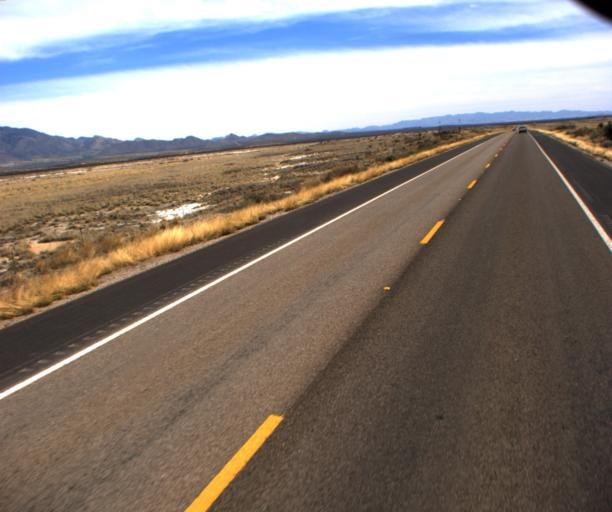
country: US
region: Arizona
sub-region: Cochise County
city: Willcox
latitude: 32.2189
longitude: -109.7877
